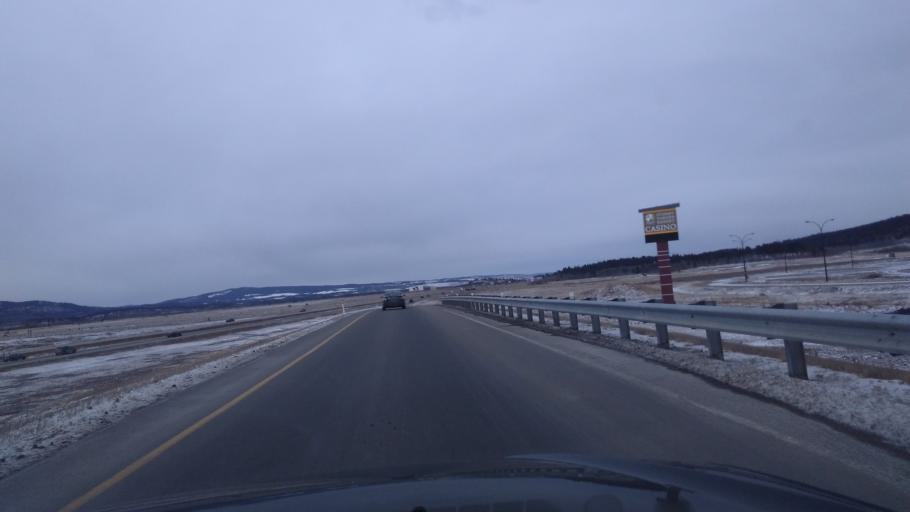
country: CA
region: Alberta
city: Canmore
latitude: 51.1029
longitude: -115.0196
